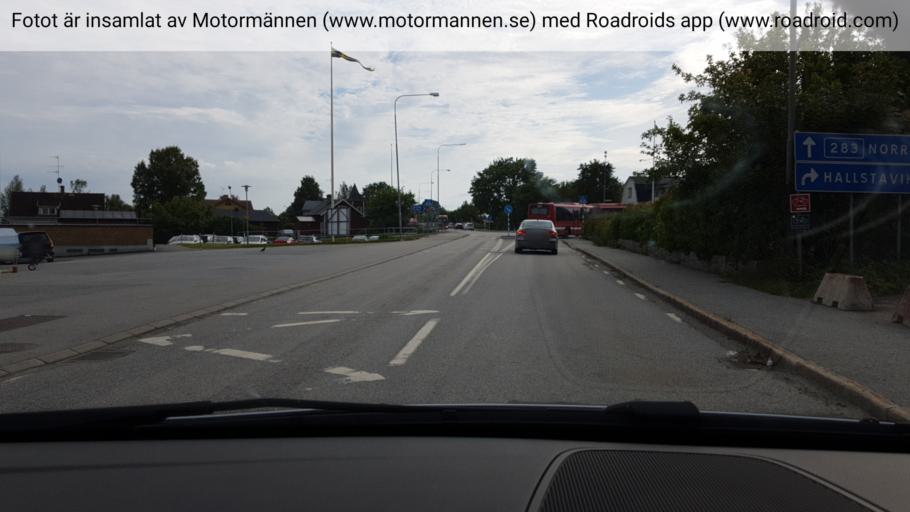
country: SE
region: Stockholm
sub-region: Norrtalje Kommun
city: Hallstavik
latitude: 59.9717
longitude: 18.8092
